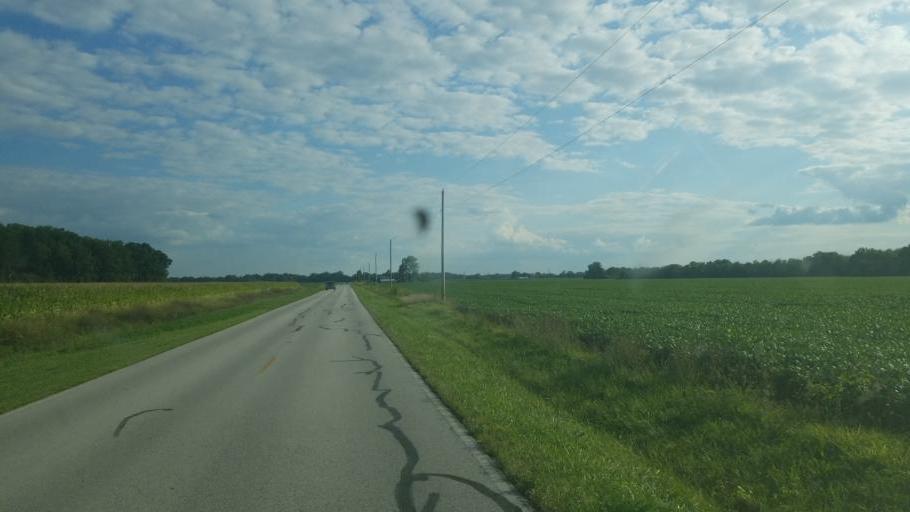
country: US
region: Ohio
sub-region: Seneca County
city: Tiffin
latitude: 41.1808
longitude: -83.1206
